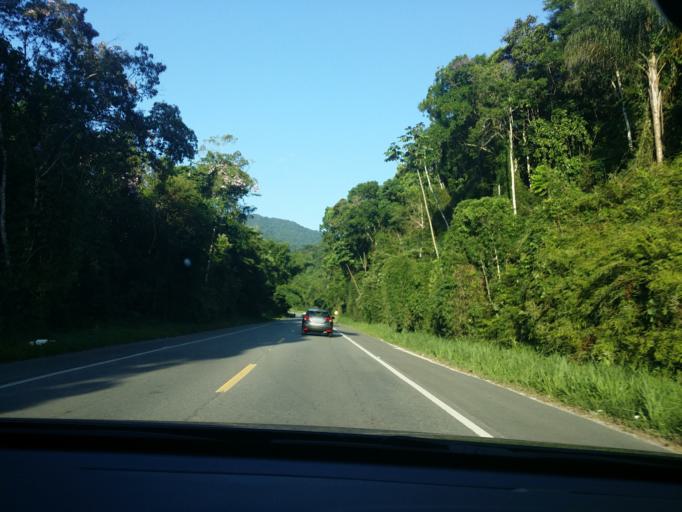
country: BR
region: Sao Paulo
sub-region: Sao Sebastiao
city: Sao Sebastiao
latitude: -23.7483
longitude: -45.7430
